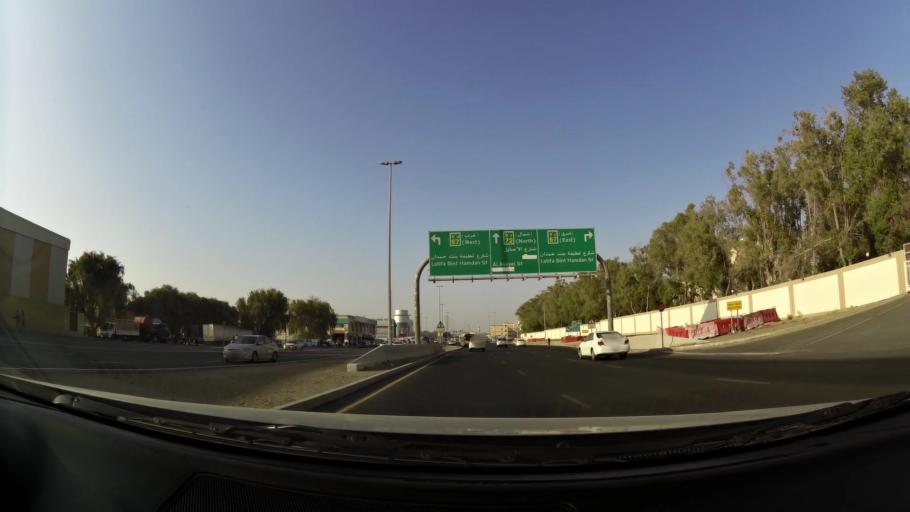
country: AE
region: Dubai
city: Dubai
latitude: 25.1460
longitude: 55.2454
